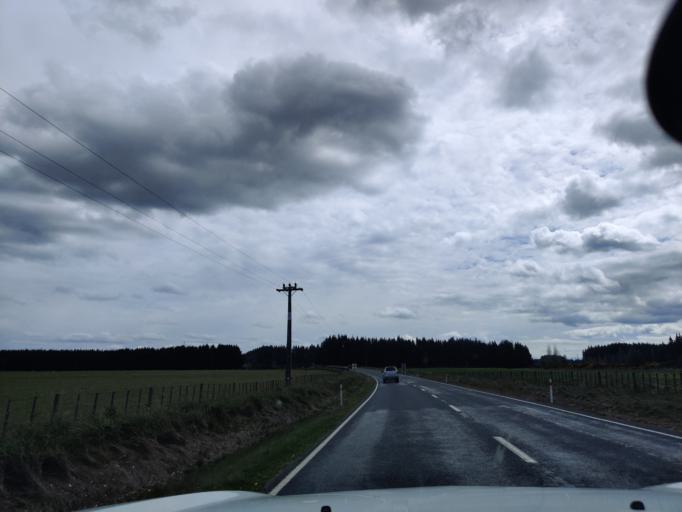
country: NZ
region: Manawatu-Wanganui
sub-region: Ruapehu District
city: Waiouru
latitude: -39.4672
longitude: 175.5842
